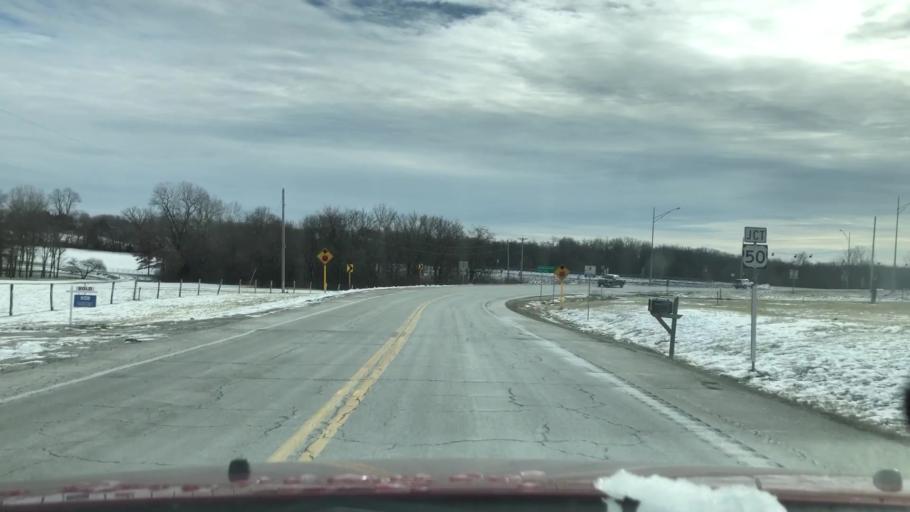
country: US
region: Missouri
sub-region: Jackson County
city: Lone Jack
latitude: 38.8718
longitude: -94.1345
